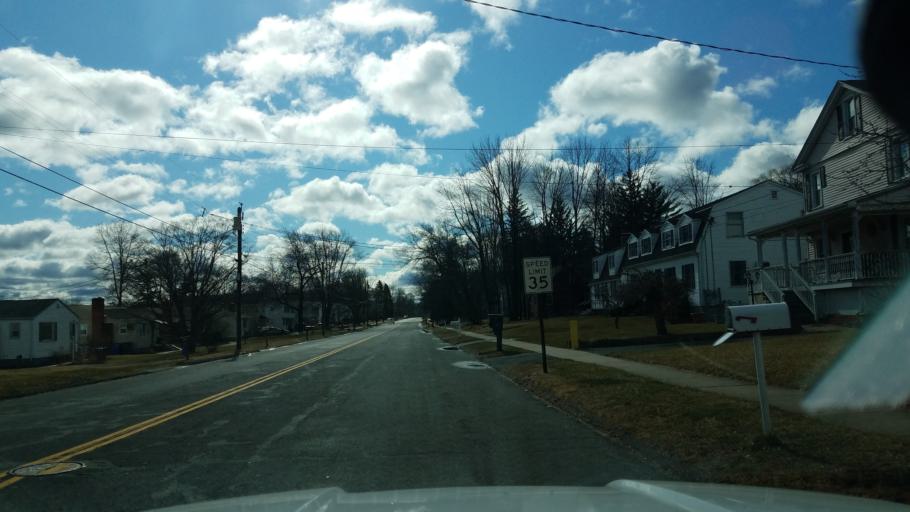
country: US
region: Connecticut
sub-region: Hartford County
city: Wethersfield
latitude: 41.6954
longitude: -72.6532
